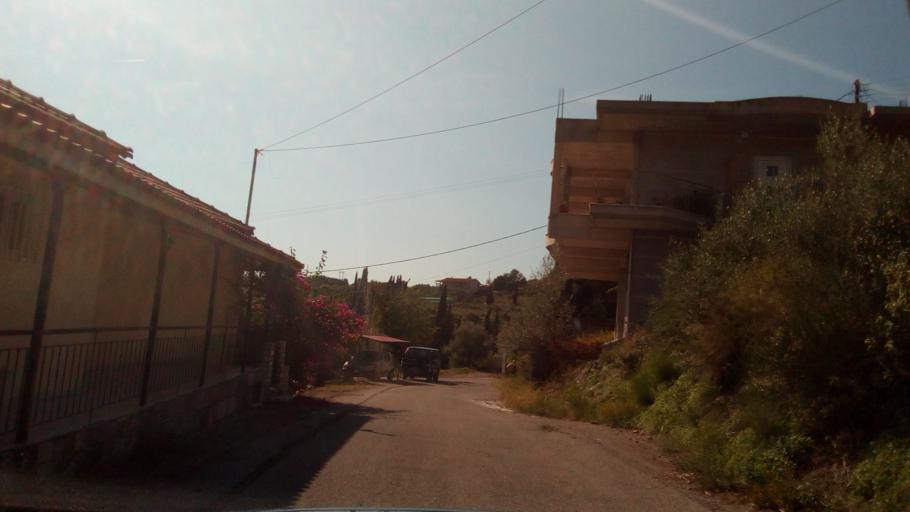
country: GR
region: West Greece
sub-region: Nomos Aitolias kai Akarnanias
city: Nafpaktos
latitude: 38.4207
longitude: 21.8688
